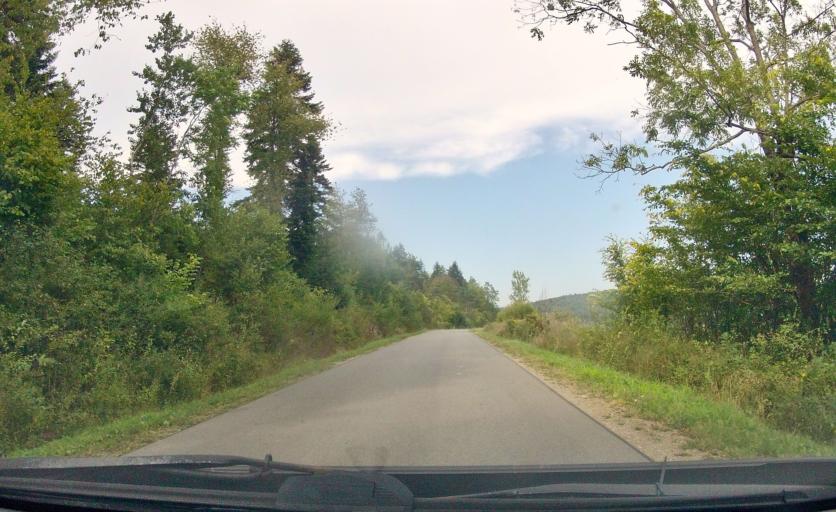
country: PL
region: Subcarpathian Voivodeship
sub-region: Powiat krosnienski
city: Dukla
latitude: 49.5049
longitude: 21.6244
